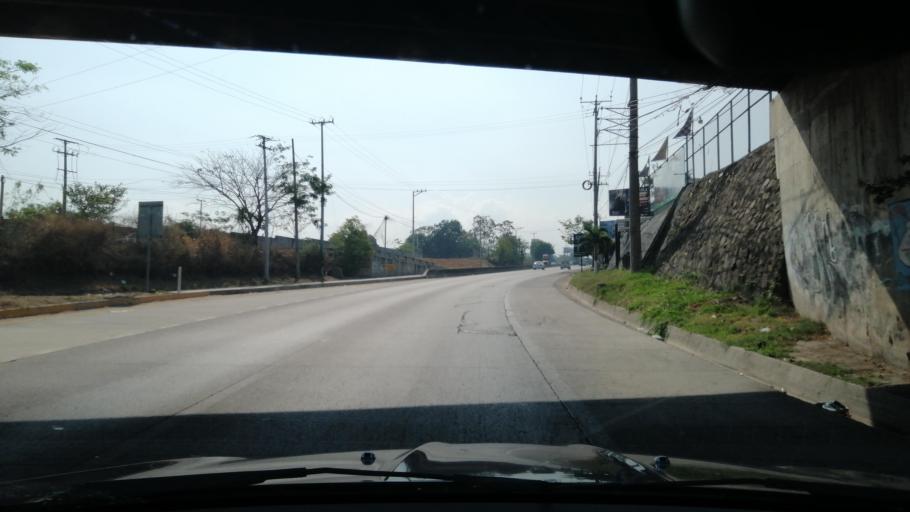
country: SV
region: La Libertad
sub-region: Distrito de Quezaltepeque
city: Quezaltepeque
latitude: 13.8045
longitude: -89.2370
